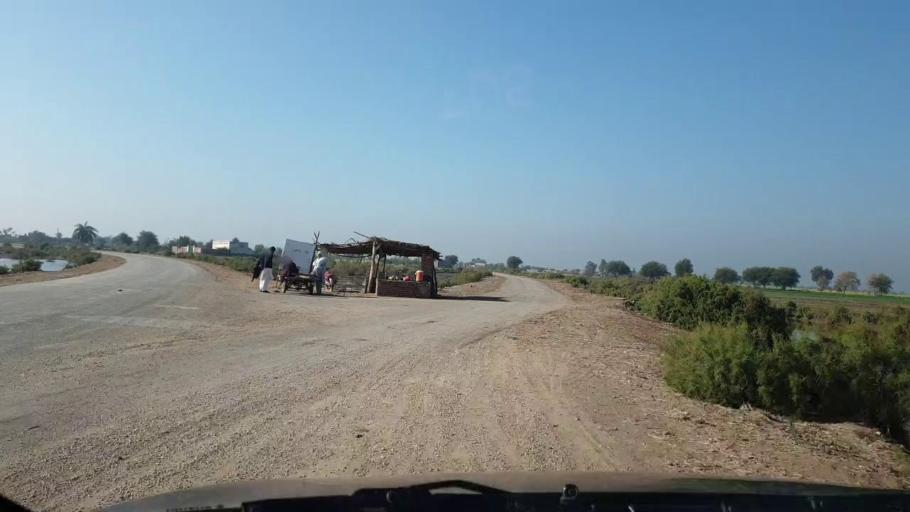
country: PK
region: Sindh
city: Sinjhoro
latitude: 26.0166
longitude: 68.7942
